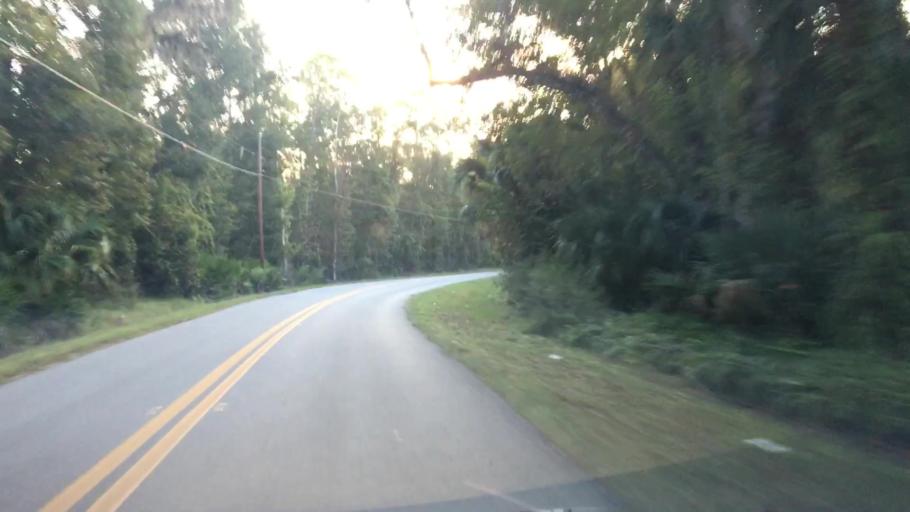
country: US
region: Florida
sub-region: Volusia County
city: Deltona
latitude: 28.8566
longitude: -81.2113
